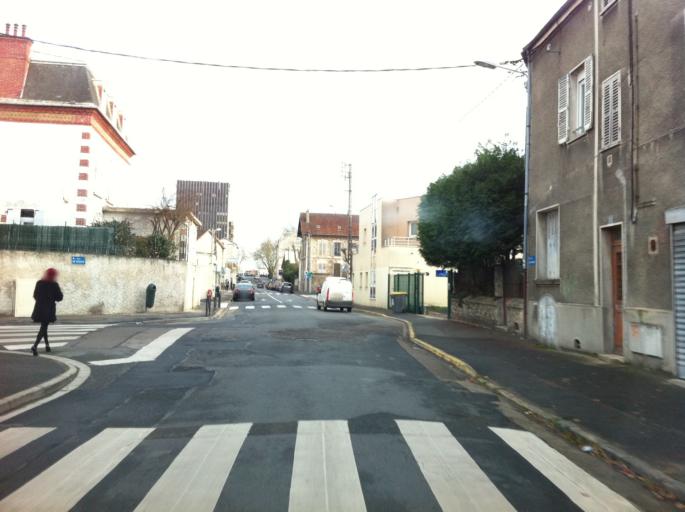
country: FR
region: Ile-de-France
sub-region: Departement de Seine-et-Marne
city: Dammarie-les-Lys
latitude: 48.5314
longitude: 2.6456
